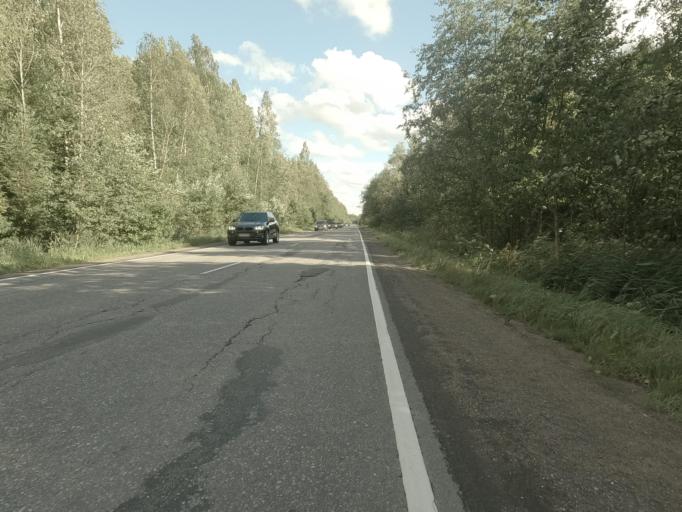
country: RU
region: Leningrad
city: Shcheglovo
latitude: 59.9935
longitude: 30.8799
